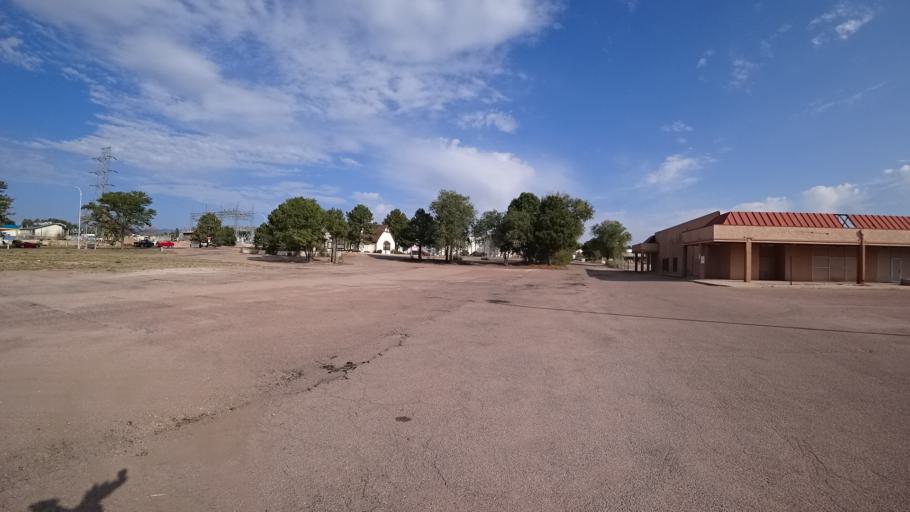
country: US
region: Colorado
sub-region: El Paso County
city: Cimarron Hills
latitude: 38.8574
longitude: -104.7553
